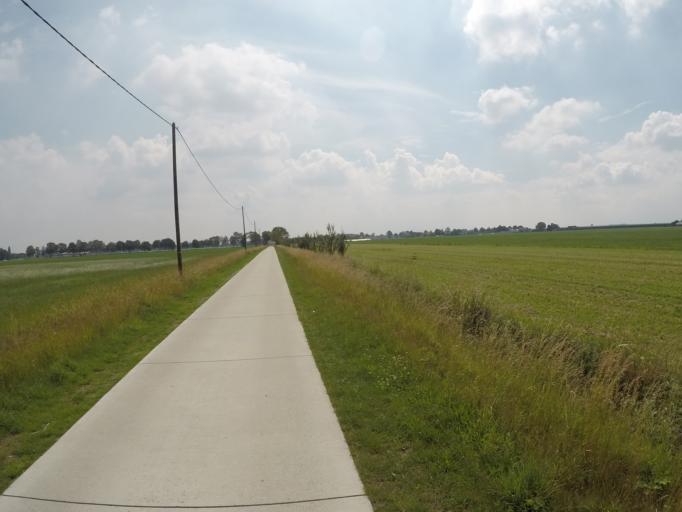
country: BE
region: Flanders
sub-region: Provincie Antwerpen
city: Rijkevorsel
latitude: 51.3648
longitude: 4.7272
